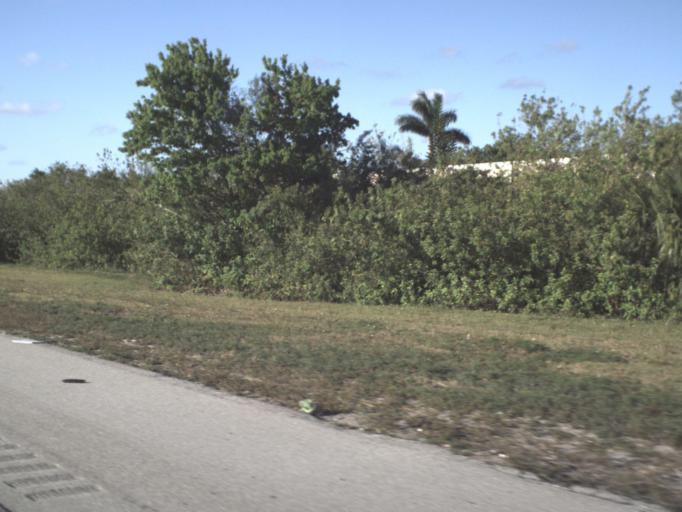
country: US
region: Florida
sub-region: Brevard County
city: Rockledge
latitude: 28.2543
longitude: -80.7253
